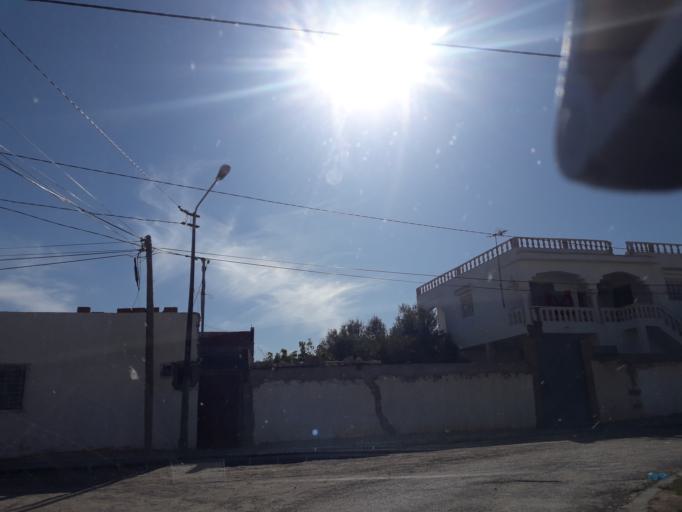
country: TN
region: Safaqis
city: Sfax
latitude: 34.7386
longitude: 10.5202
